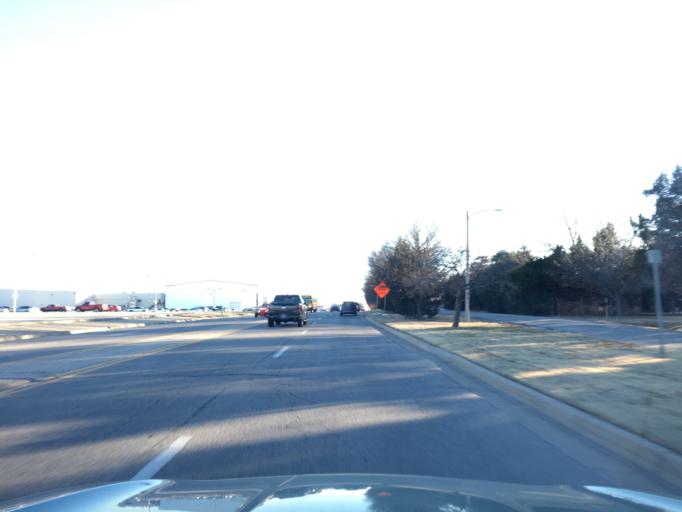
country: US
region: Kansas
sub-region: Sedgwick County
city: Bellaire
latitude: 37.6910
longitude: -97.2263
